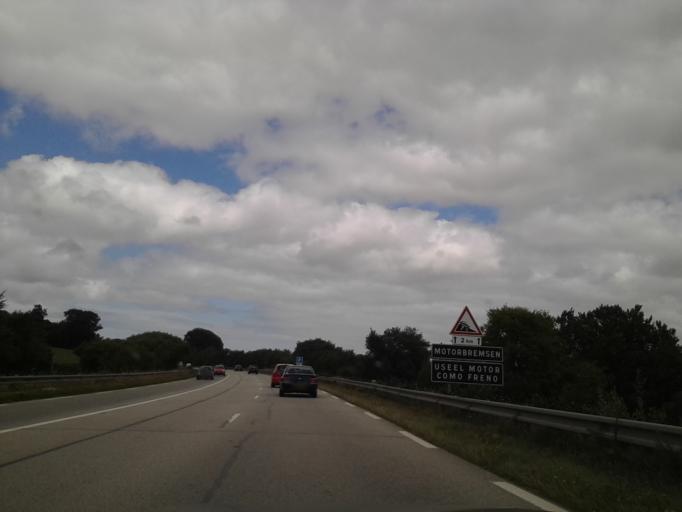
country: FR
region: Lower Normandy
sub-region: Departement de la Manche
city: La Glacerie
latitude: 49.6119
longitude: -1.5843
